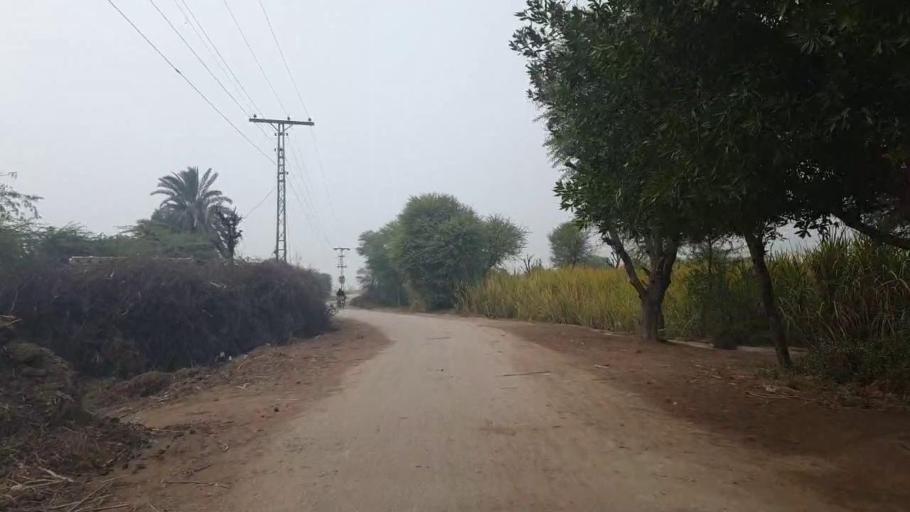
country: PK
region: Sindh
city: Tando Adam
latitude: 25.8145
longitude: 68.7163
